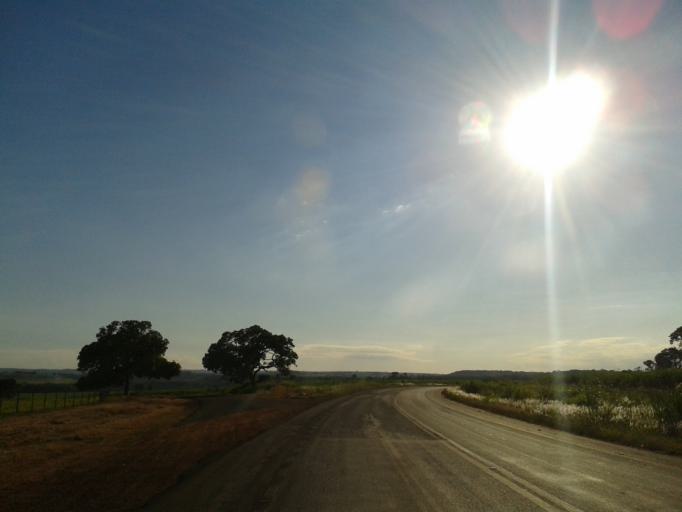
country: BR
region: Minas Gerais
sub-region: Centralina
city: Centralina
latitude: -18.7065
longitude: -49.2918
